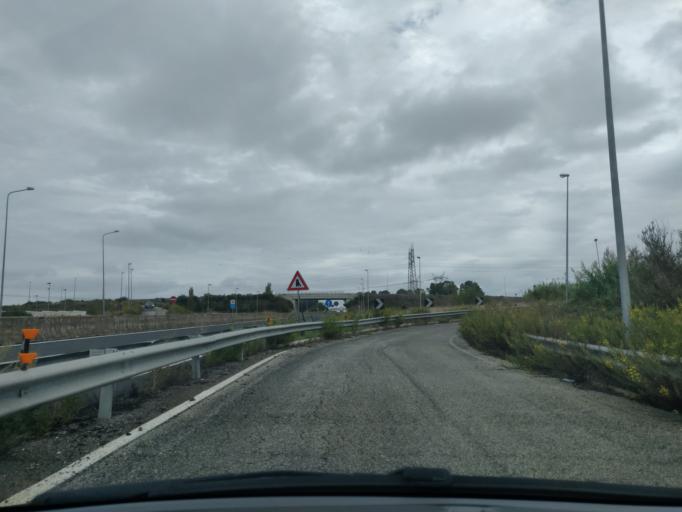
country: IT
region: Latium
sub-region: Citta metropolitana di Roma Capitale
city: Aurelia
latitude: 42.1273
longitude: 11.7920
